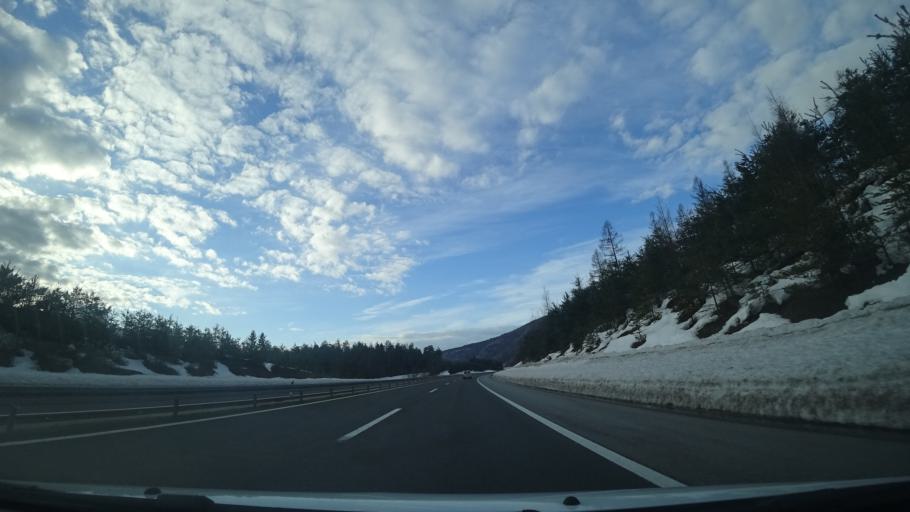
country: HR
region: Karlovacka
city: Ostarije
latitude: 45.2033
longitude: 15.2651
